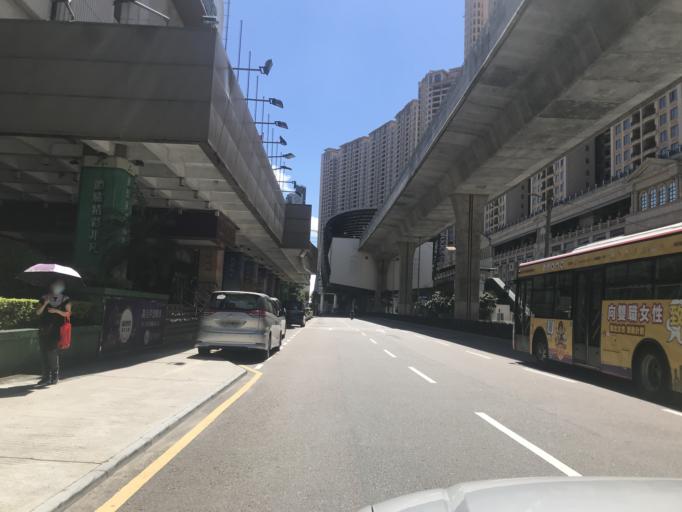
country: MO
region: Macau
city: Macau
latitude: 22.1570
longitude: 113.5487
